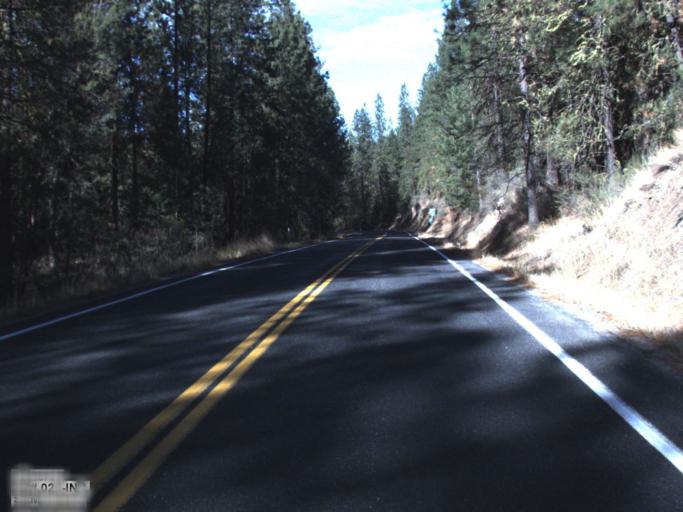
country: US
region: Washington
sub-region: Stevens County
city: Kettle Falls
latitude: 48.1960
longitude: -118.1705
